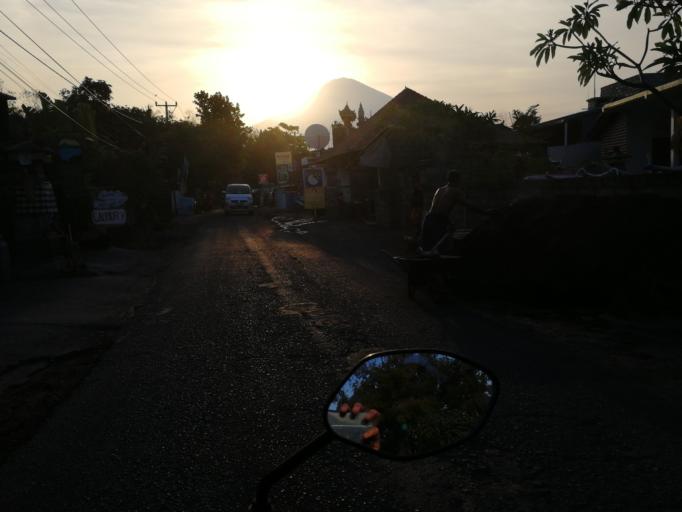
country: ID
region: Bali
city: Biaslantang Kaler
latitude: -8.3356
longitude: 115.6513
